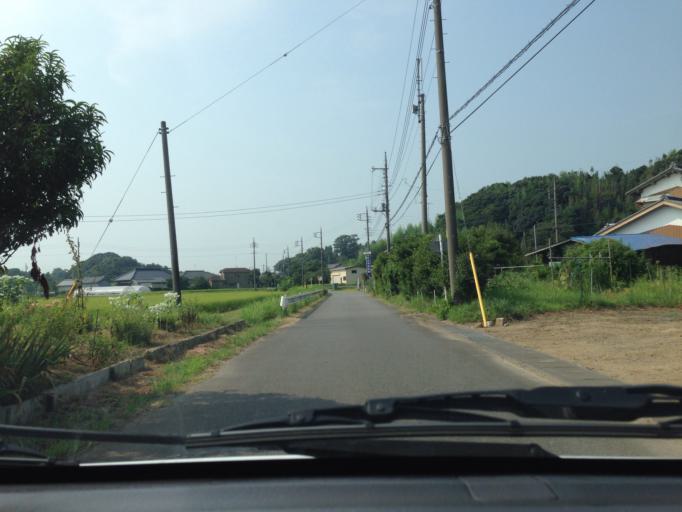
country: JP
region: Ibaraki
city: Inashiki
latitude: 36.0204
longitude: 140.3564
